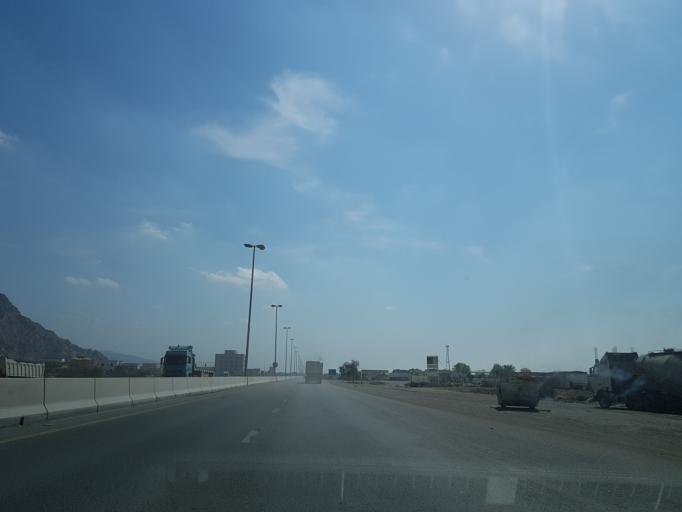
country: AE
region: Ra's al Khaymah
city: Ras al-Khaimah
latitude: 25.8545
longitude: 56.0204
